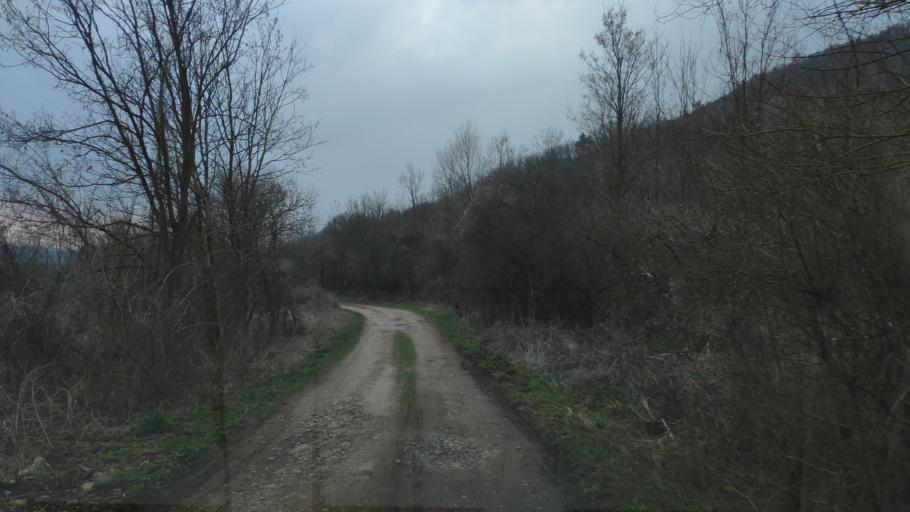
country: SK
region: Kosicky
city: Roznava
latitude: 48.6604
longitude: 20.3818
